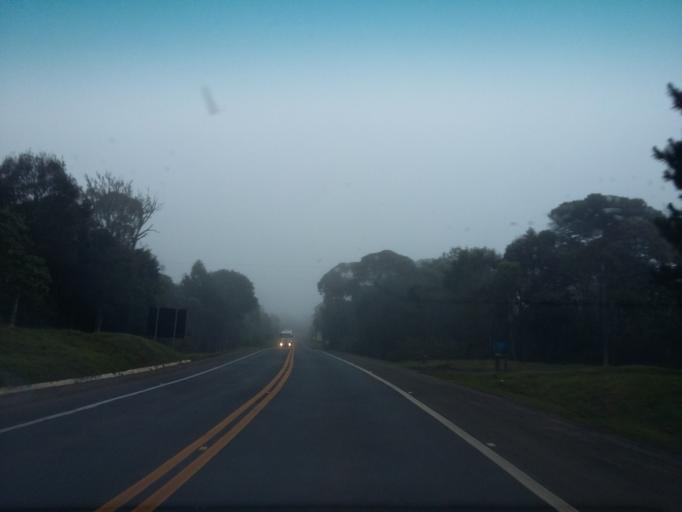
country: BR
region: Santa Catarina
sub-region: Curitibanos
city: Curitibanos
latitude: -27.2955
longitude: -50.4294
